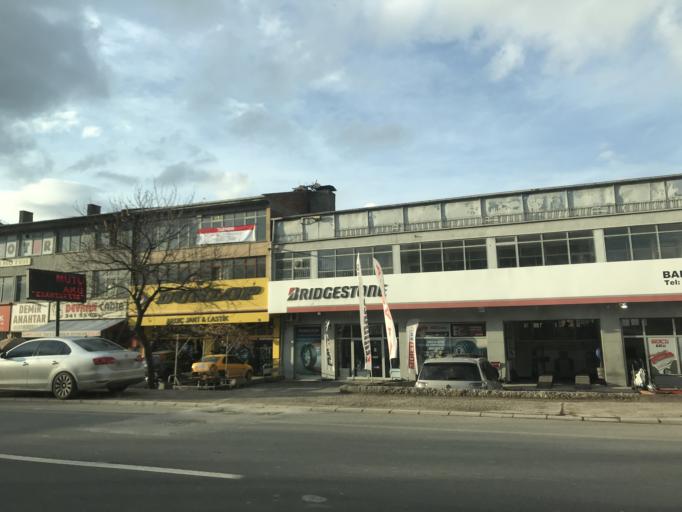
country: TR
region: Ankara
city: Ankara
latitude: 39.9544
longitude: 32.8407
